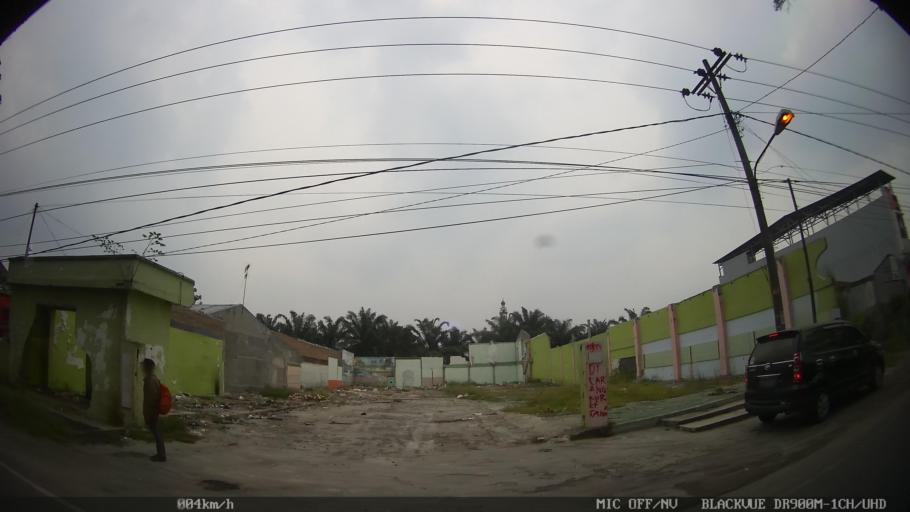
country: ID
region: North Sumatra
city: Medan
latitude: 3.5704
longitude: 98.7244
